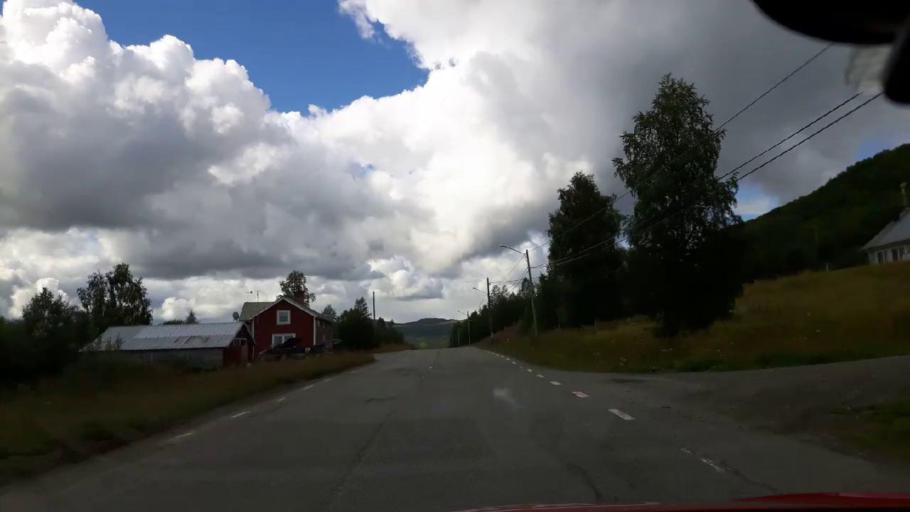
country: NO
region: Nordland
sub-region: Hattfjelldal
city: Hattfjelldal
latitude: 65.0594
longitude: 14.7899
